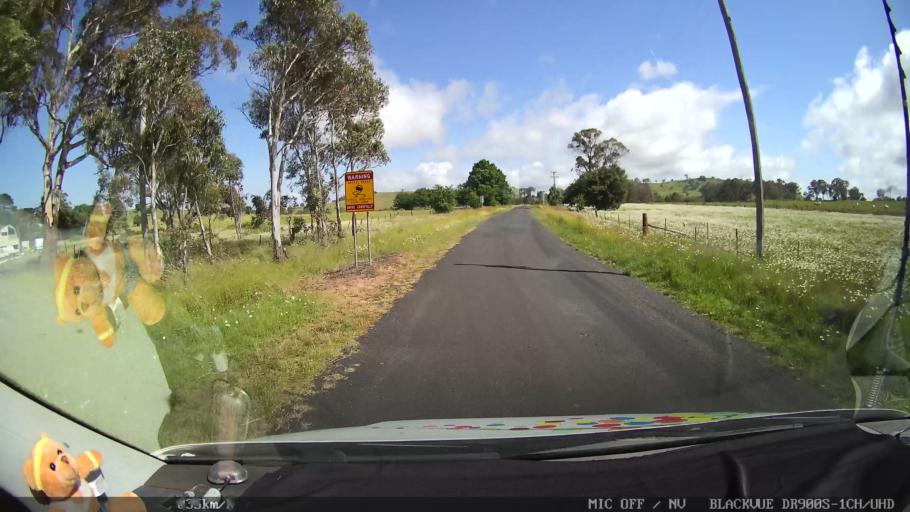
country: AU
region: New South Wales
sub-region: Guyra
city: Guyra
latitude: -30.0168
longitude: 151.6578
